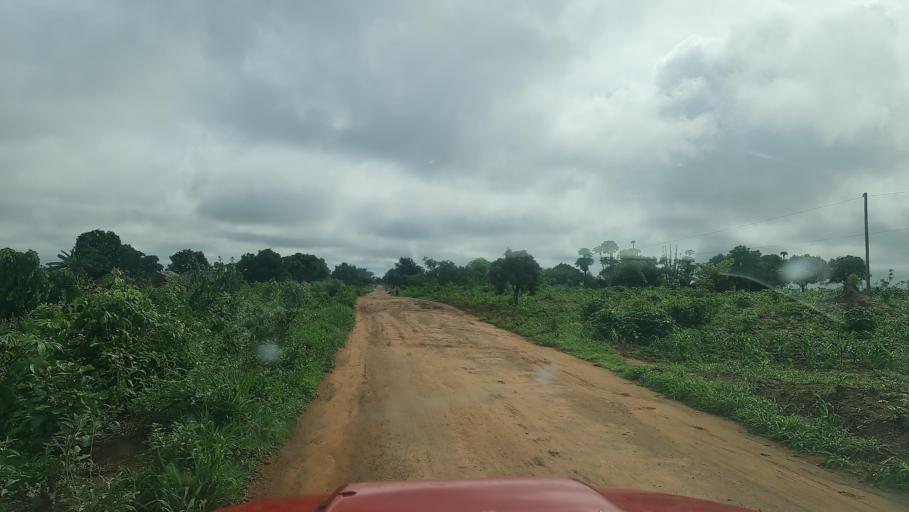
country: MW
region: Southern Region
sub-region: Nsanje District
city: Nsanje
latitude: -17.2221
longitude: 35.6675
